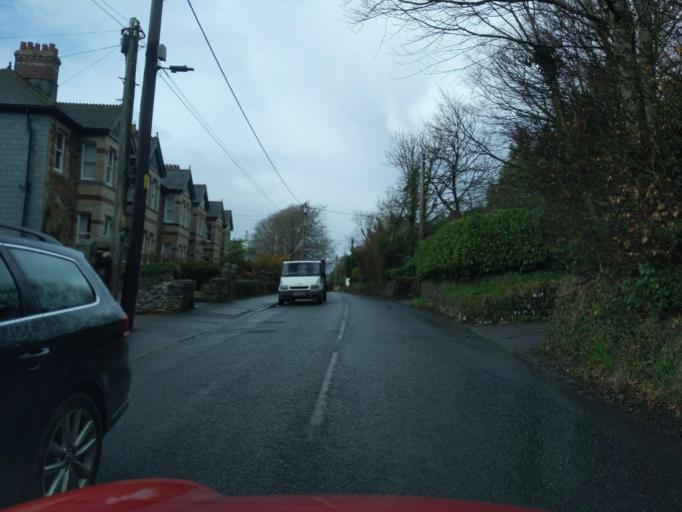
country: GB
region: England
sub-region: Devon
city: Tavistock
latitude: 50.5390
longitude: -4.1400
